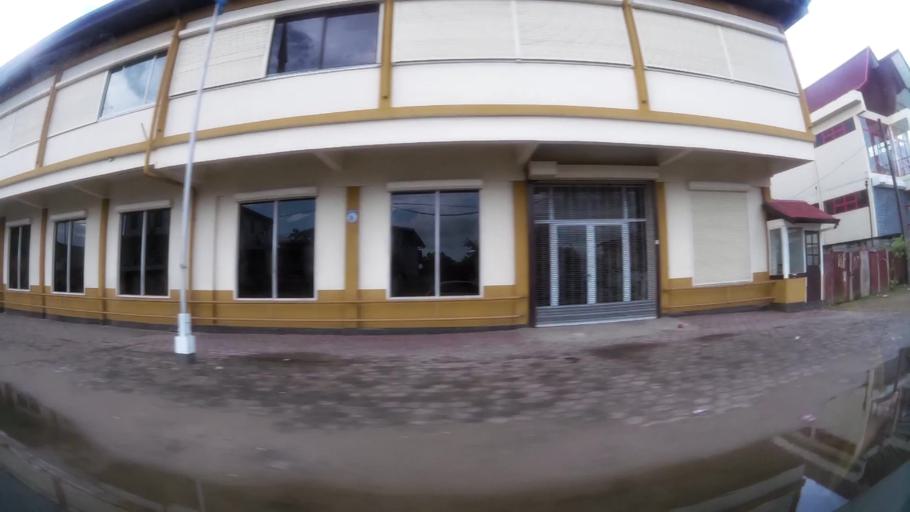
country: SR
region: Paramaribo
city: Paramaribo
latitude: 5.8213
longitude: -55.1705
